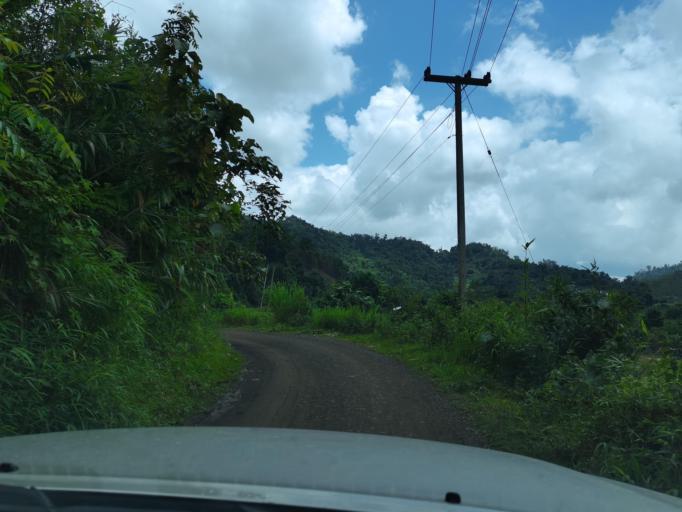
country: LA
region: Loungnamtha
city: Muang Long
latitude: 20.7496
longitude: 101.0183
